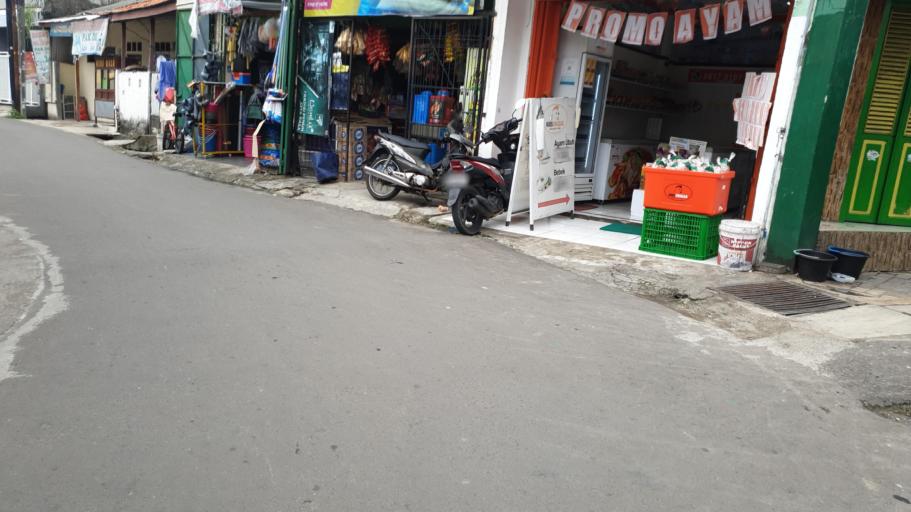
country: ID
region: Banten
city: South Tangerang
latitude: -6.2578
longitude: 106.7841
